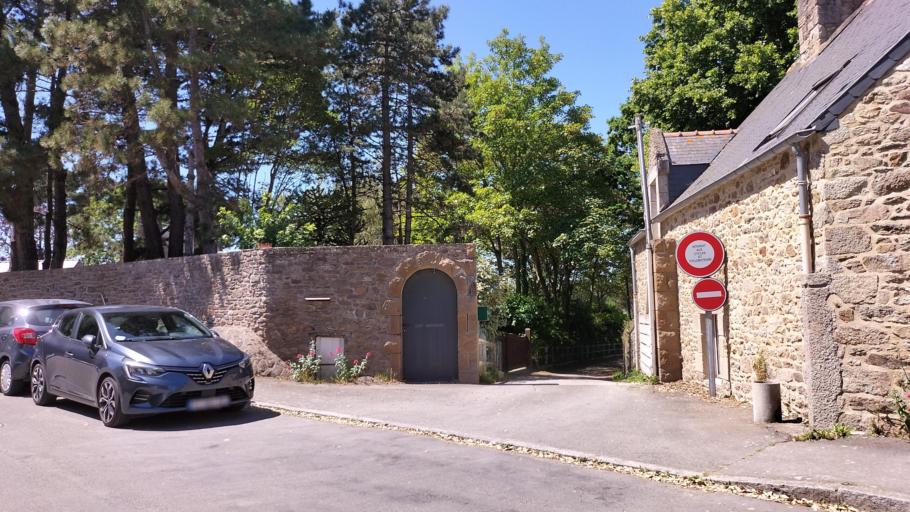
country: FR
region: Brittany
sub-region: Departement d'Ille-et-Vilaine
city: Dinard
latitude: 48.6385
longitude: -2.0755
